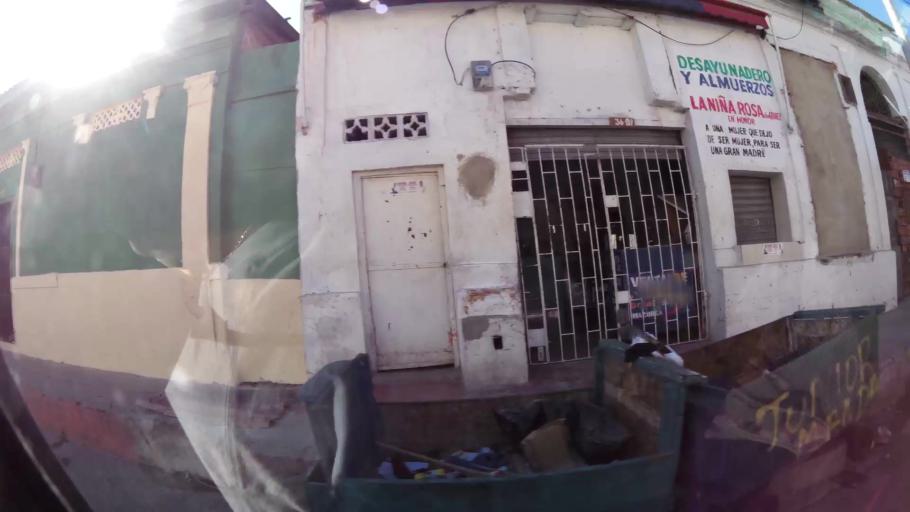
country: CO
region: Atlantico
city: Barranquilla
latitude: 10.9763
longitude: -74.7786
